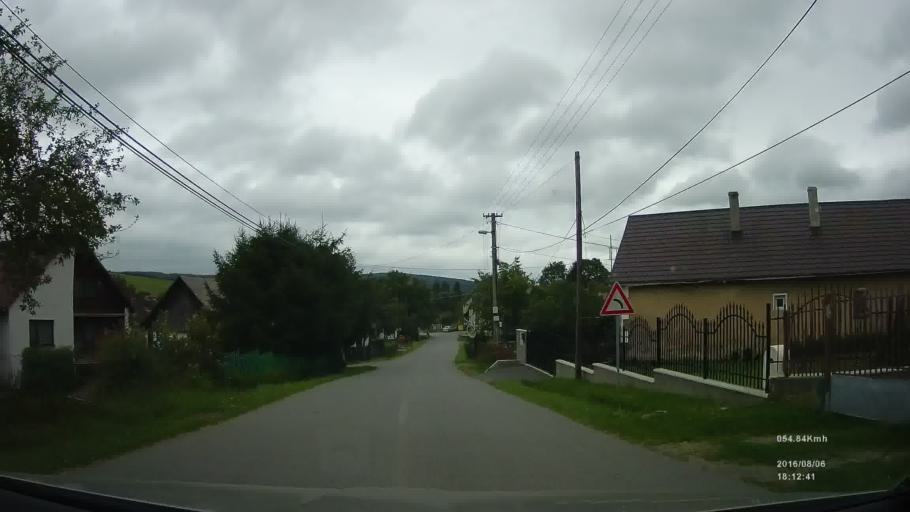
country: SK
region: Presovsky
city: Svidnik
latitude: 49.3629
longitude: 21.5805
